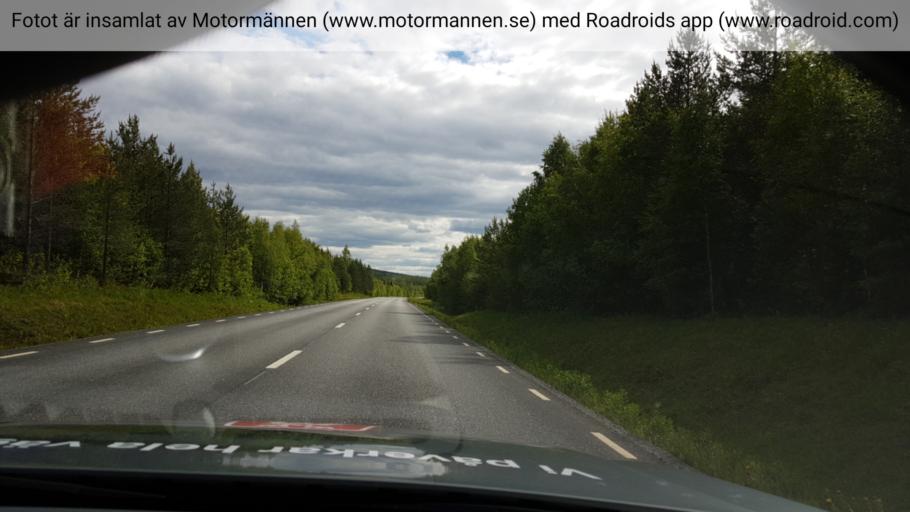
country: SE
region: Jaemtland
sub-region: Stroemsunds Kommun
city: Stroemsund
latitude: 64.0402
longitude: 15.5393
